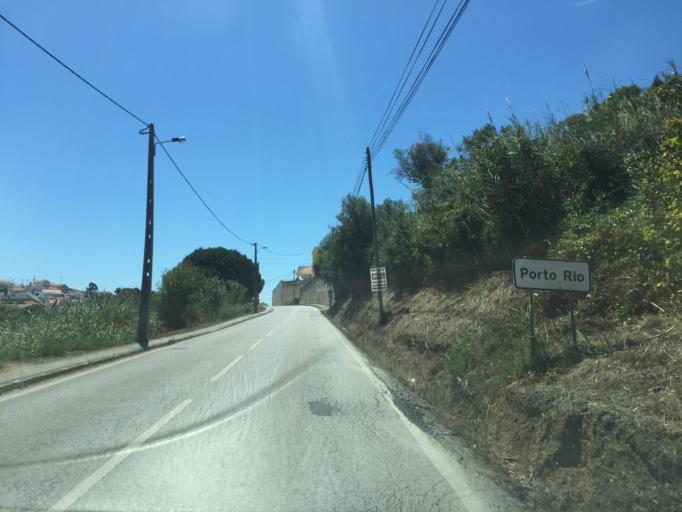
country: PT
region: Lisbon
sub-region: Torres Vedras
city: A dos Cunhados
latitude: 39.1808
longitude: -9.3233
